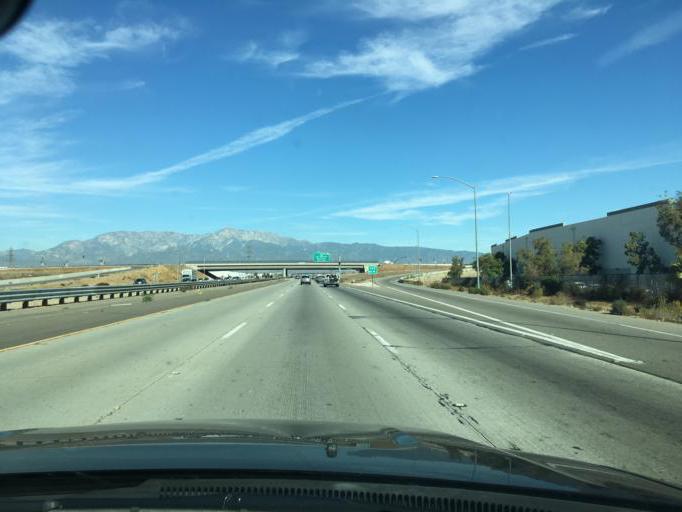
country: US
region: California
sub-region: Riverside County
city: Mira Loma
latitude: 33.9984
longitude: -117.5502
